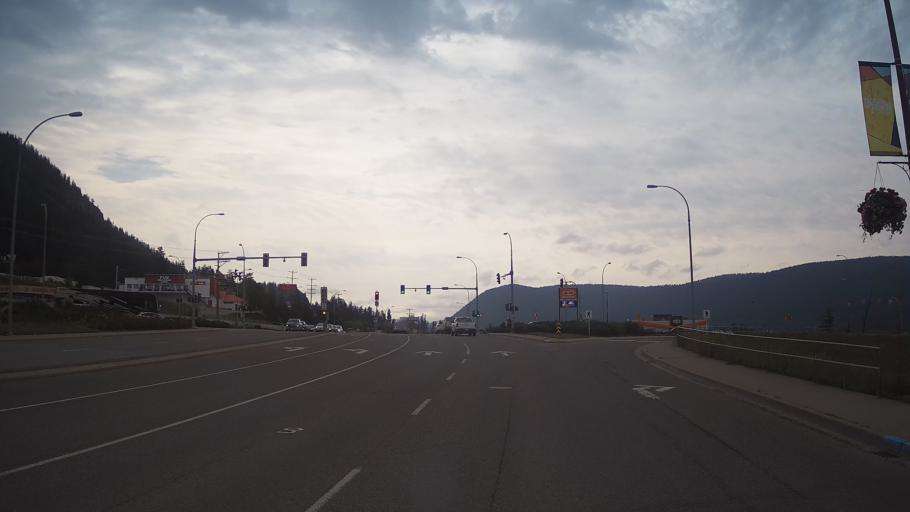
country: CA
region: British Columbia
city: Williams Lake
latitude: 52.1277
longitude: -122.1291
